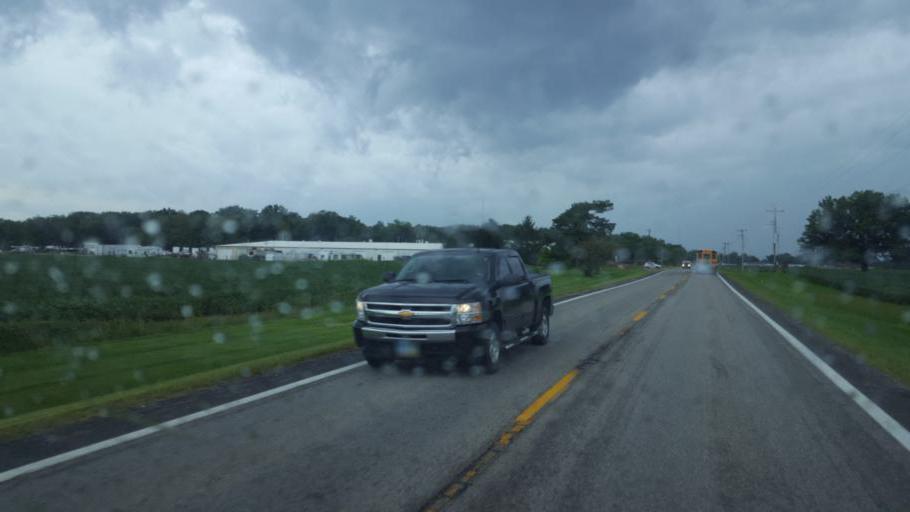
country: US
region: Ohio
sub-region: Delaware County
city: Delaware
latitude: 40.3154
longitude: -83.0372
